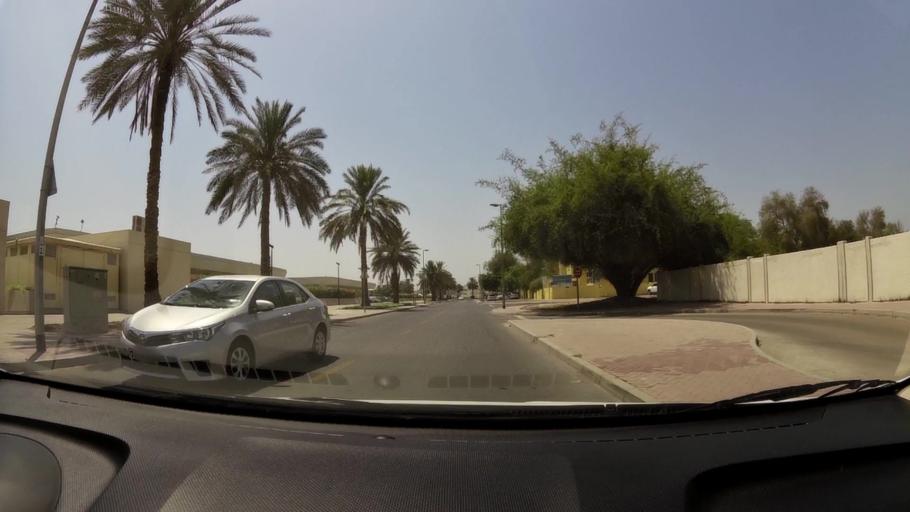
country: AE
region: Ash Shariqah
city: Sharjah
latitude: 25.2836
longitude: 55.3427
